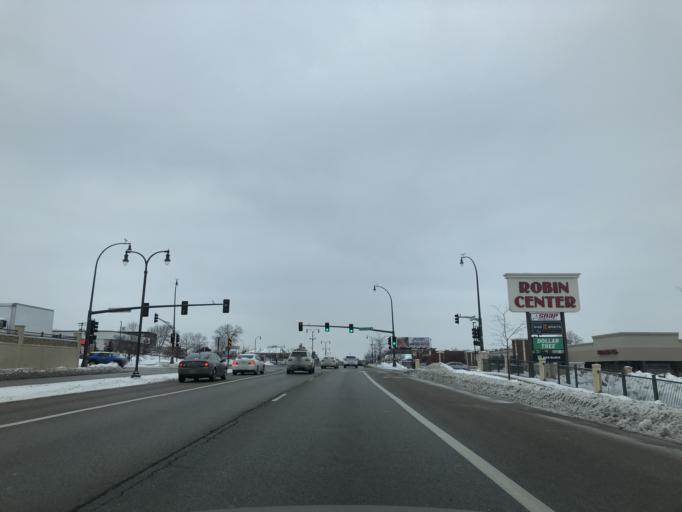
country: US
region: Minnesota
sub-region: Hennepin County
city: Robbinsdale
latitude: 45.0300
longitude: -93.3356
